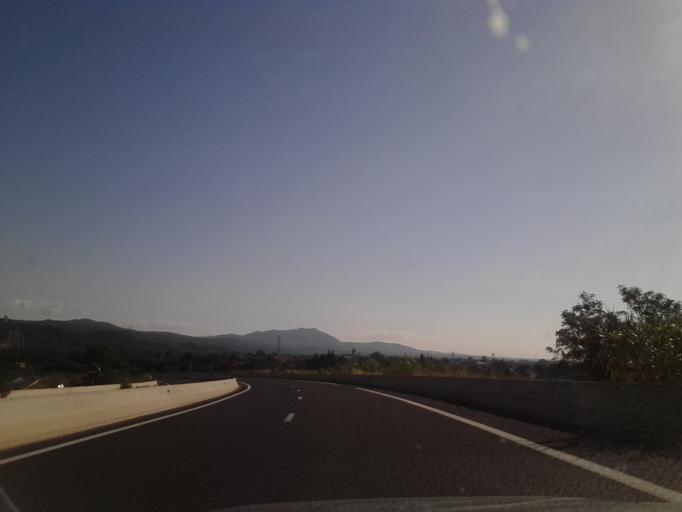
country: FR
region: Languedoc-Roussillon
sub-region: Departement des Pyrenees-Orientales
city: Ille-sur-Tet
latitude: 42.6610
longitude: 2.6008
